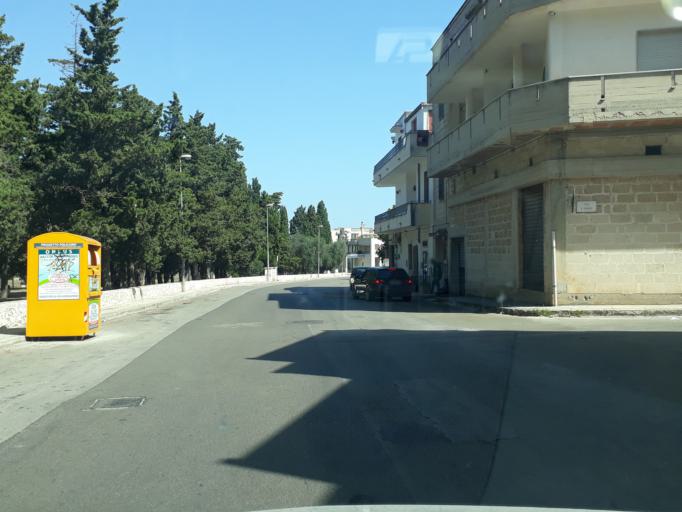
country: IT
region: Apulia
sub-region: Provincia di Brindisi
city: Carovigno
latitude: 40.7110
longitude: 17.6567
